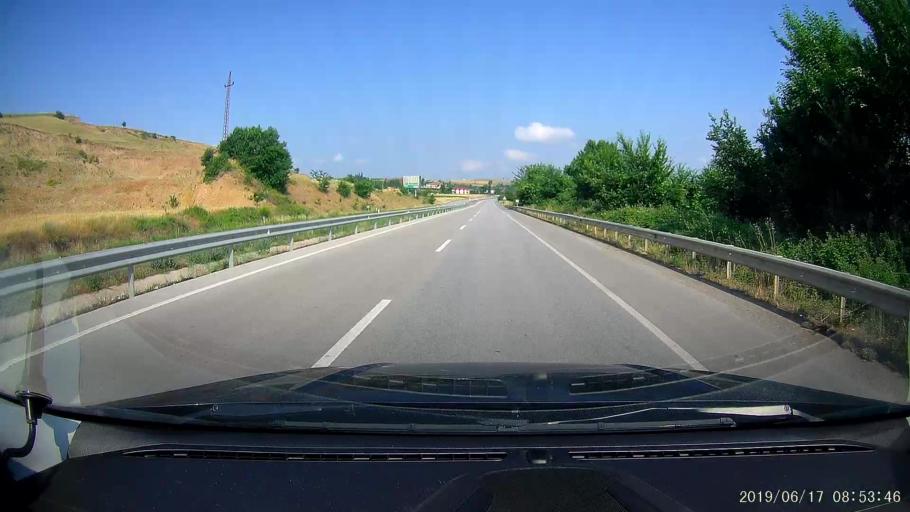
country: TR
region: Tokat
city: Erbaa
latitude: 40.7127
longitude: 36.4747
